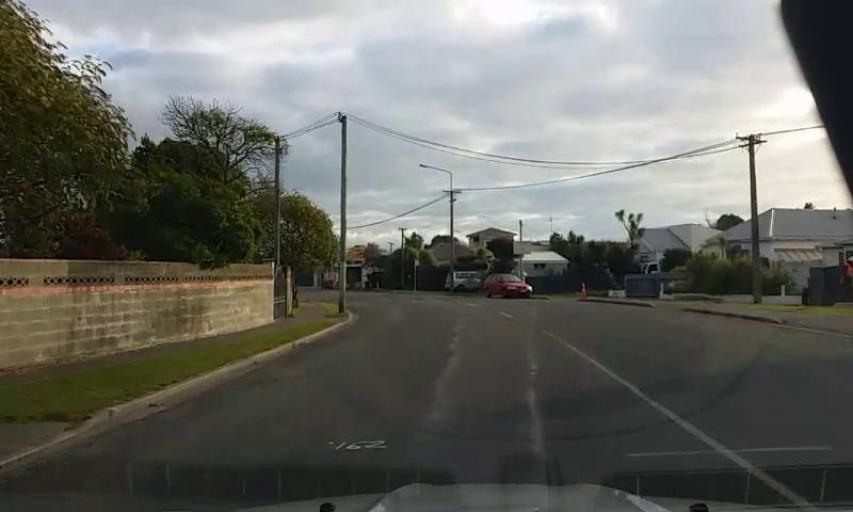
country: NZ
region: Canterbury
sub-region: Christchurch City
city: Christchurch
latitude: -43.5189
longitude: 172.7309
